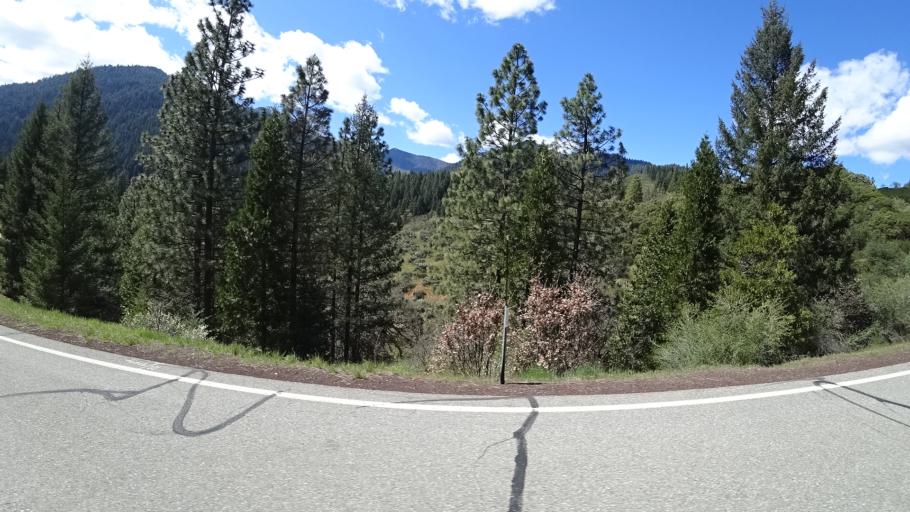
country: US
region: California
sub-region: Trinity County
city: Weaverville
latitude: 40.8199
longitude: -122.8914
